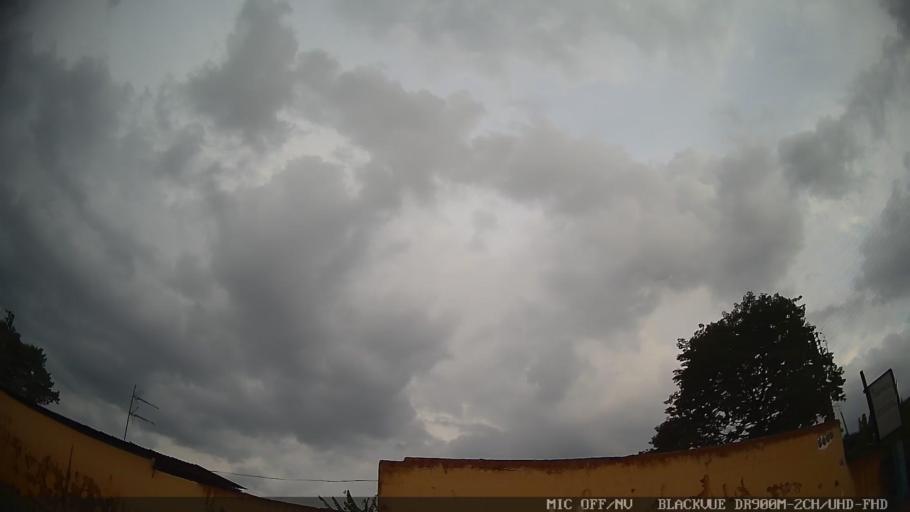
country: BR
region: Sao Paulo
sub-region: Braganca Paulista
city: Braganca Paulista
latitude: -22.9354
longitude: -46.5357
